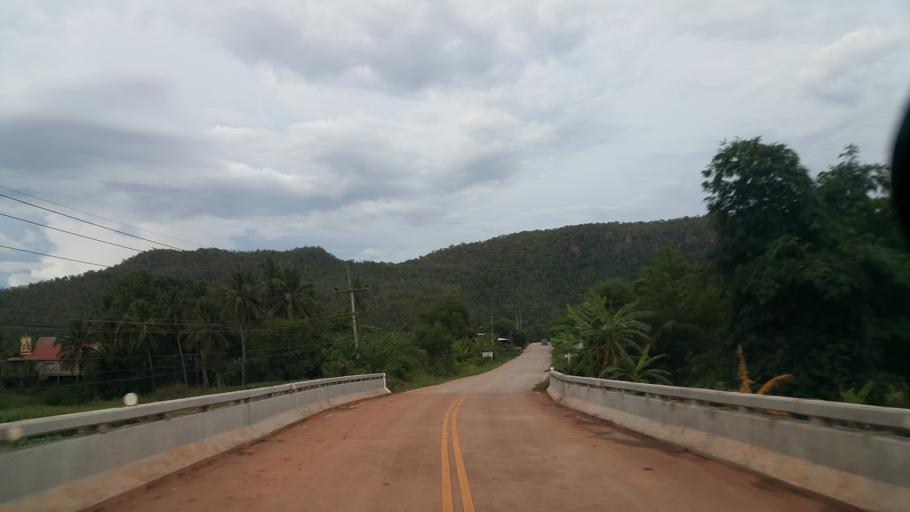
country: TH
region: Loei
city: Na Haeo
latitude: 17.4935
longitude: 101.1780
